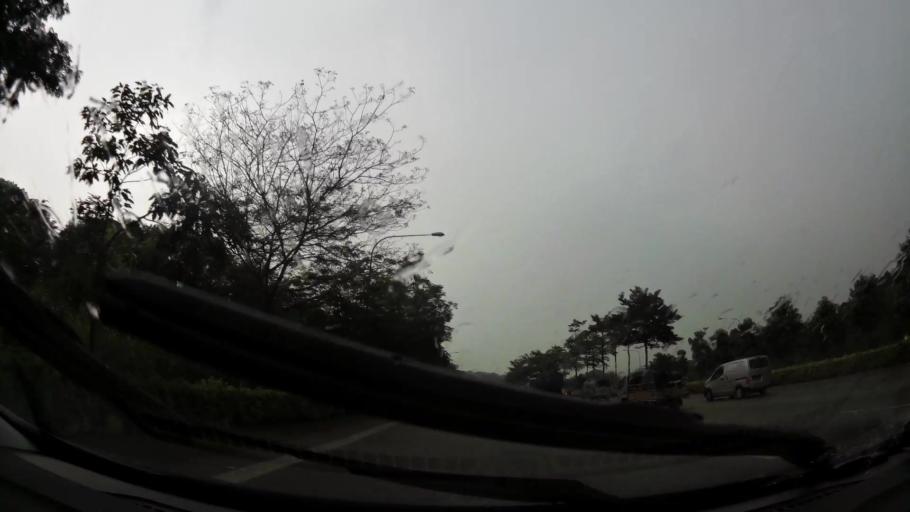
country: MY
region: Johor
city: Kampung Pasir Gudang Baru
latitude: 1.3931
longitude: 103.8298
